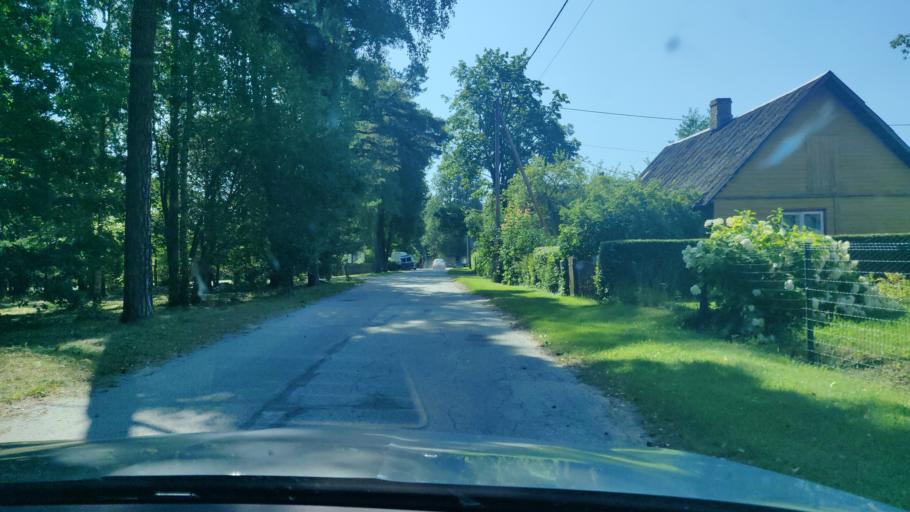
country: EE
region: Tartu
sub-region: Elva linn
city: Elva
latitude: 58.2163
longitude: 26.4082
